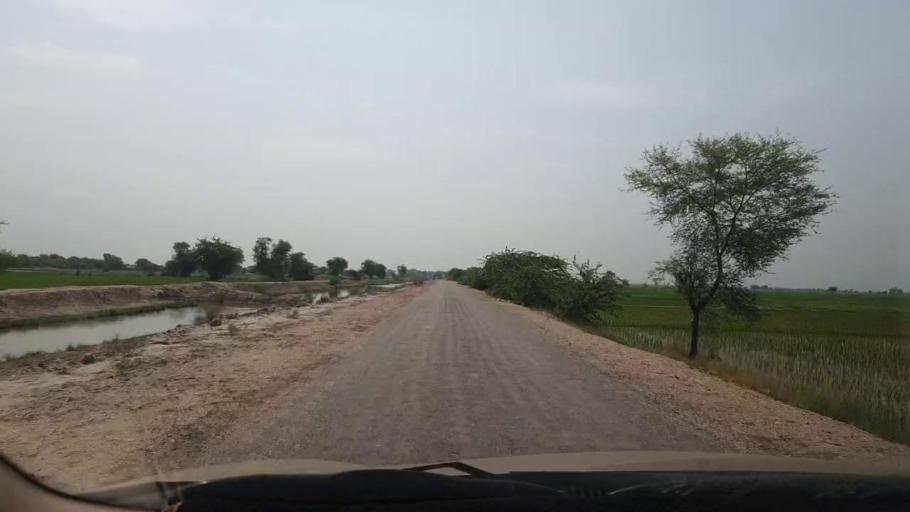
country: PK
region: Sindh
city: Goth Garelo
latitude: 27.5141
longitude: 68.1064
